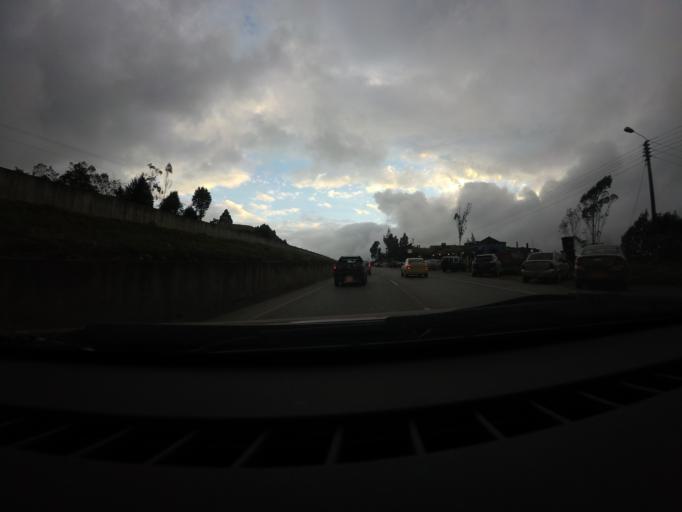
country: CO
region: Boyaca
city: Samaca
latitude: 5.4309
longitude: -73.4501
